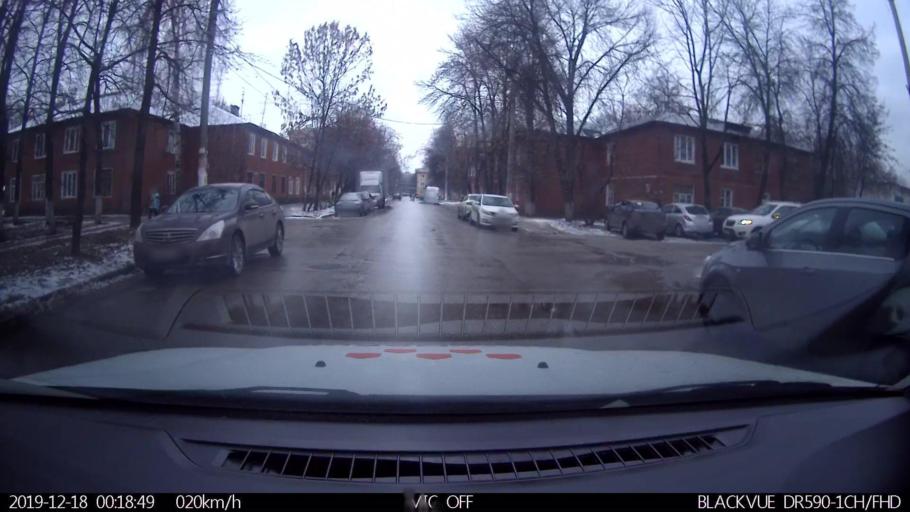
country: RU
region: Nizjnij Novgorod
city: Nizhniy Novgorod
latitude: 56.3306
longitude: 43.8823
